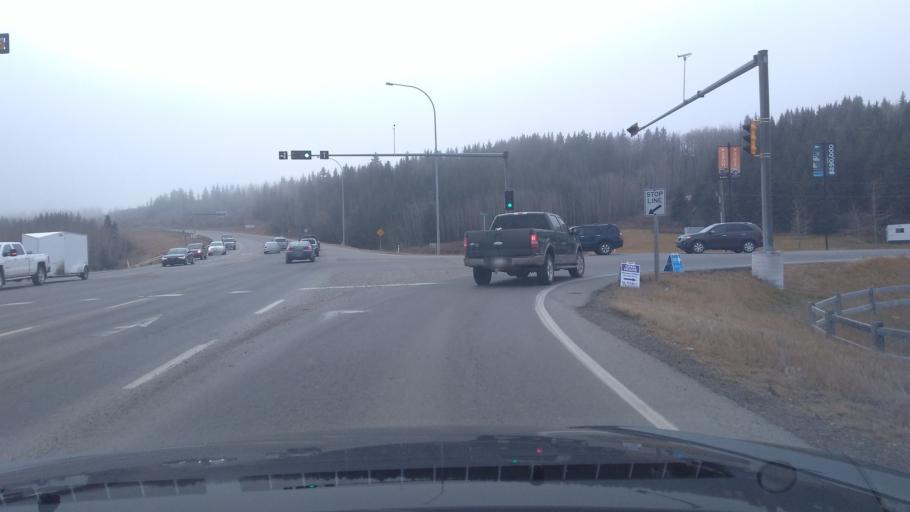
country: CA
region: Alberta
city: Cochrane
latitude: 51.1812
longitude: -114.4876
